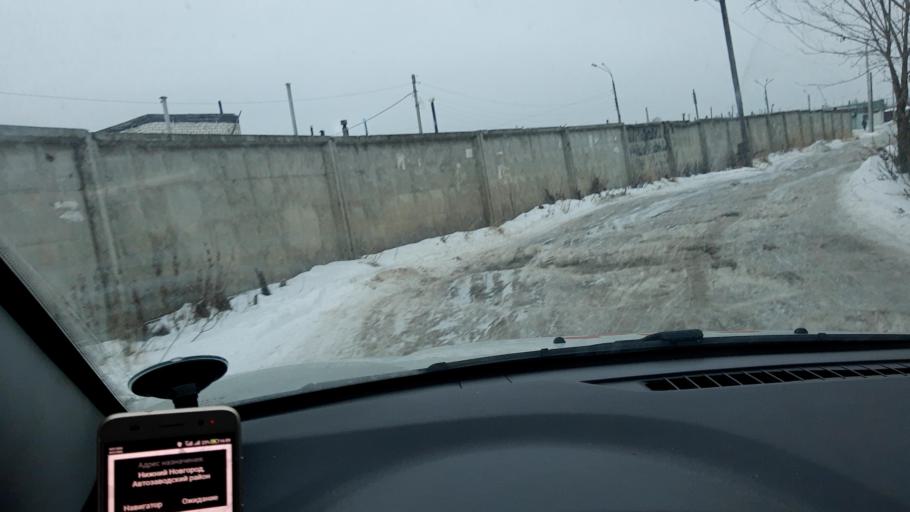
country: RU
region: Nizjnij Novgorod
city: Gorbatovka
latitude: 56.2519
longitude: 43.8324
